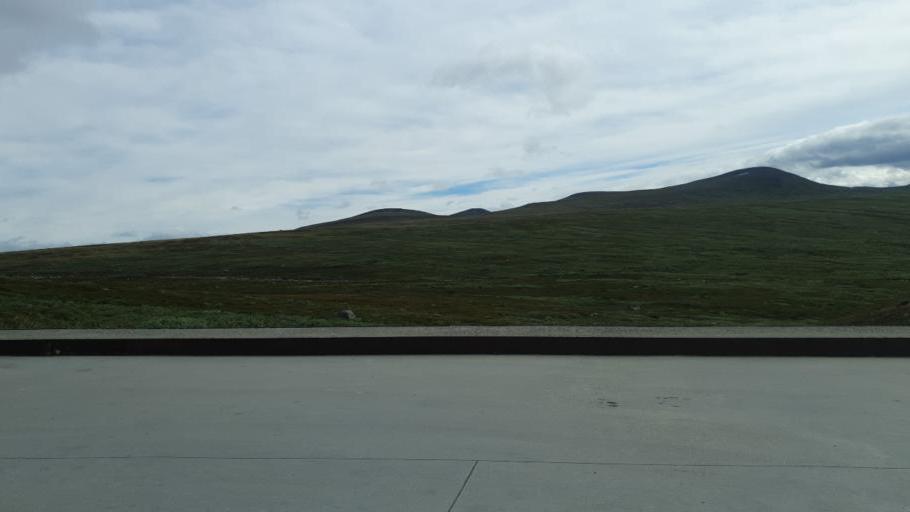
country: NO
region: Oppland
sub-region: Vestre Slidre
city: Slidre
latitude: 61.3431
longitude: 8.8129
